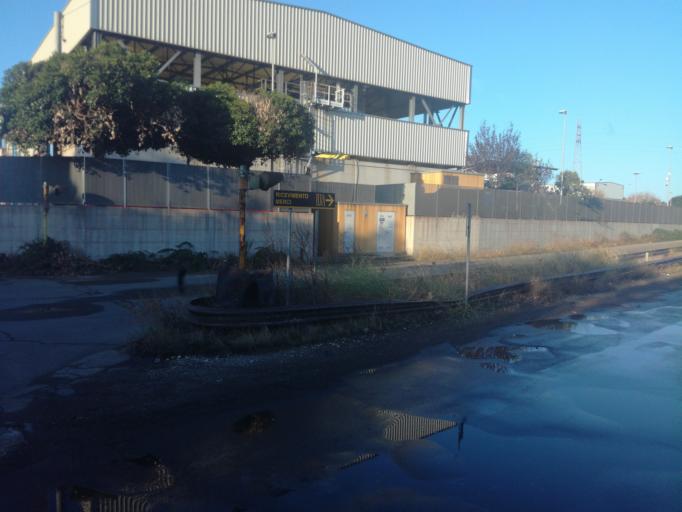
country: IT
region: Apulia
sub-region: Provincia di Taranto
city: Statte
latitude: 40.4985
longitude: 17.1979
